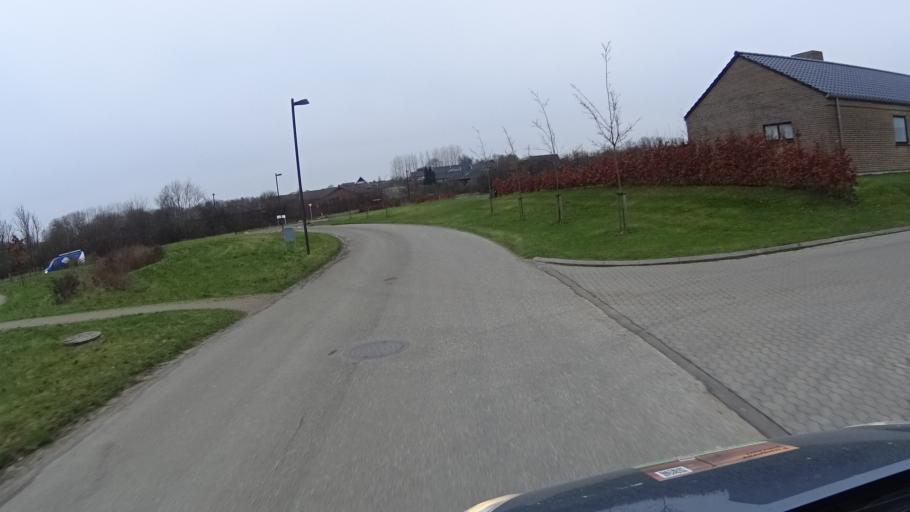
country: DK
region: South Denmark
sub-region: Vejle Kommune
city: Vejle
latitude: 55.7298
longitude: 9.6177
